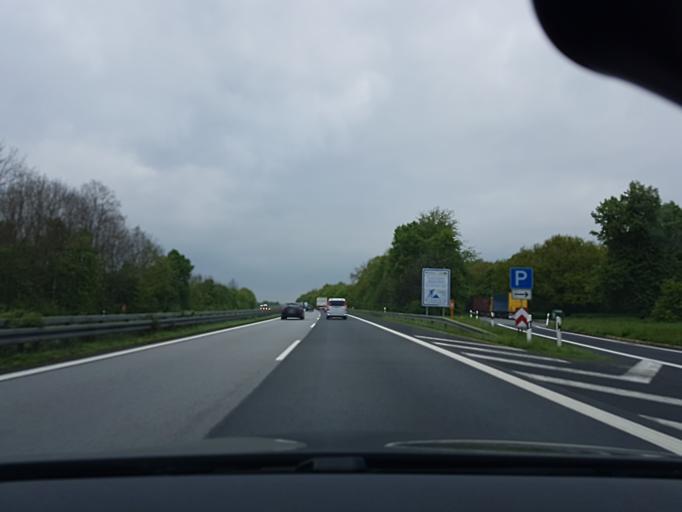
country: DE
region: Bavaria
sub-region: Regierungsbezirk Unterfranken
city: Kurnach
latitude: 49.8300
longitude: 10.0403
